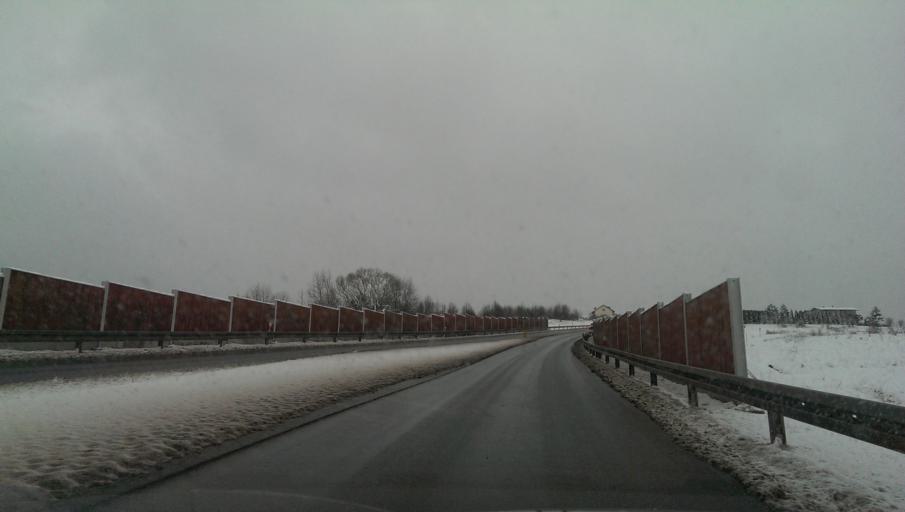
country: PL
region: Subcarpathian Voivodeship
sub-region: Powiat brzozowski
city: Brzozow
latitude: 49.7002
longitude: 22.0358
